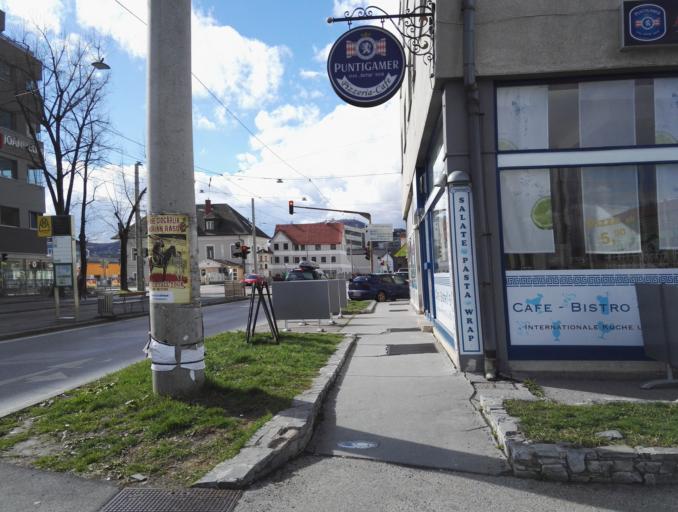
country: AT
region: Styria
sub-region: Graz Stadt
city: Wetzelsdorf
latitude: 47.0703
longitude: 15.4100
